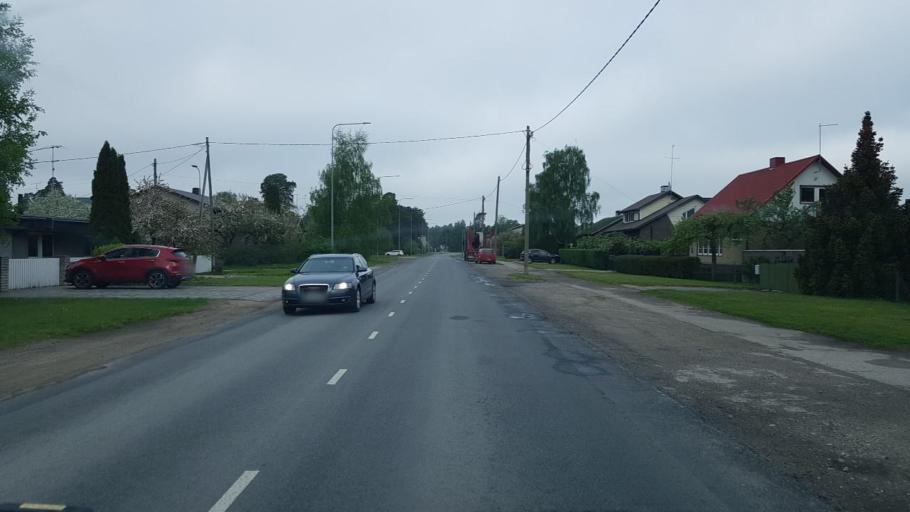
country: EE
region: Laeaene
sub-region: Haapsalu linn
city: Haapsalu
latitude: 58.9297
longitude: 23.5318
